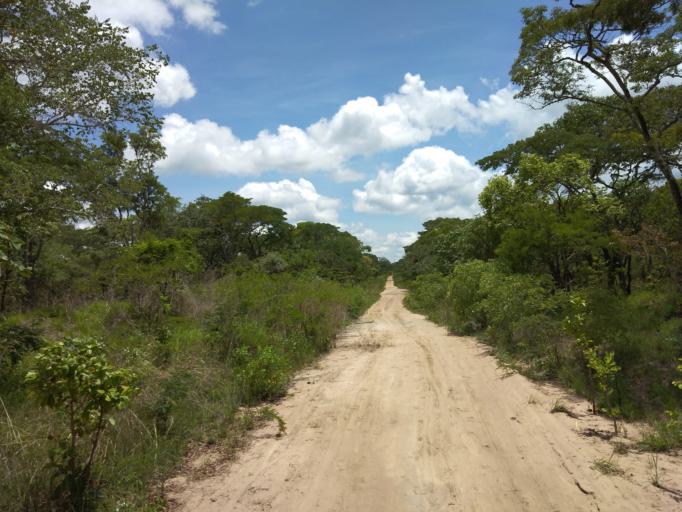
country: ZM
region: Central
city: Mkushi
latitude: -13.9454
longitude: 29.8703
